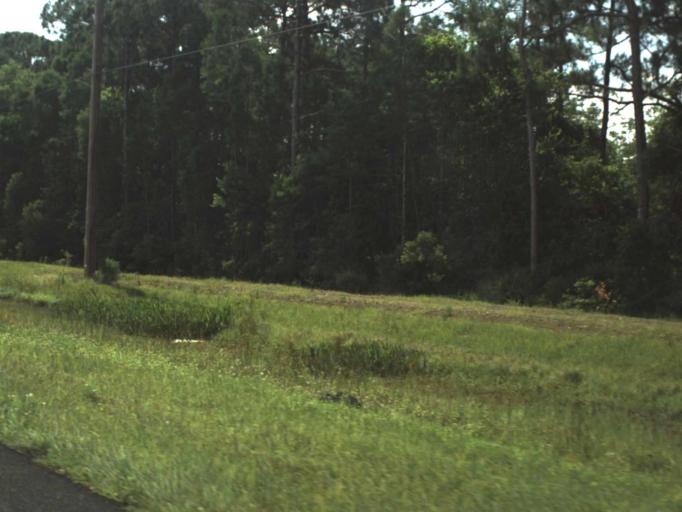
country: US
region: Florida
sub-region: Volusia County
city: Glencoe
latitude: 29.0123
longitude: -81.0037
